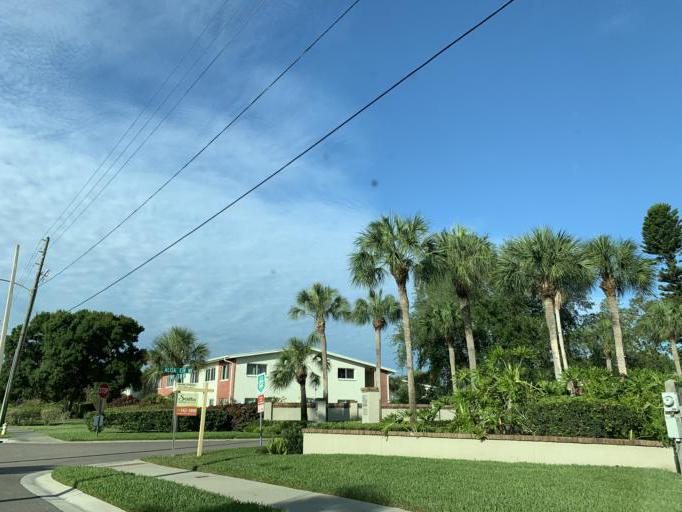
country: US
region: Florida
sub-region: Pinellas County
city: Gandy
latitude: 27.8152
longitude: -82.5984
